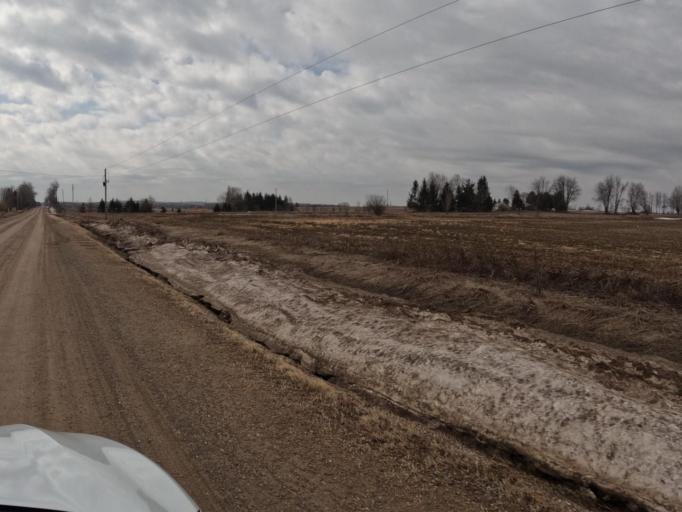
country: CA
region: Ontario
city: Orangeville
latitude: 43.9237
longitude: -80.1863
